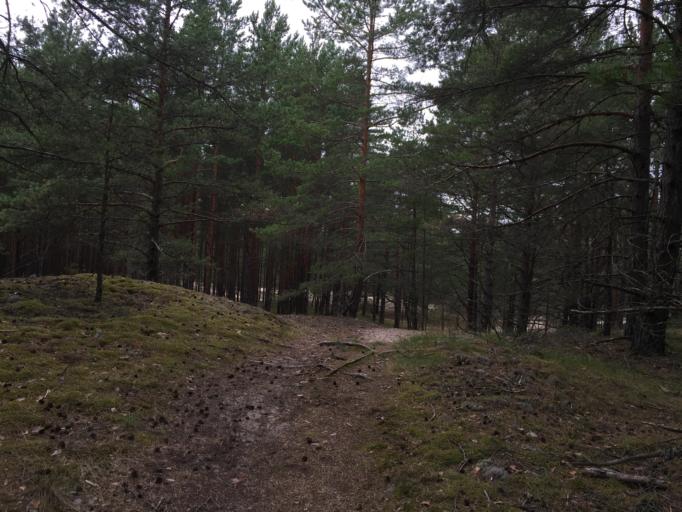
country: LV
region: Riga
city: Jaunciems
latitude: 57.1024
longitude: 24.1841
